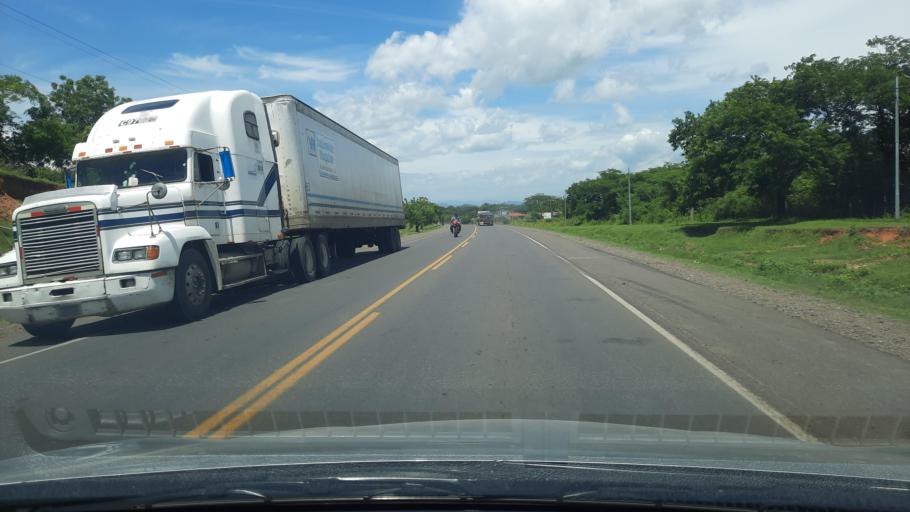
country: NI
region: Chinandega
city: Somotillo
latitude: 13.0566
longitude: -86.9232
